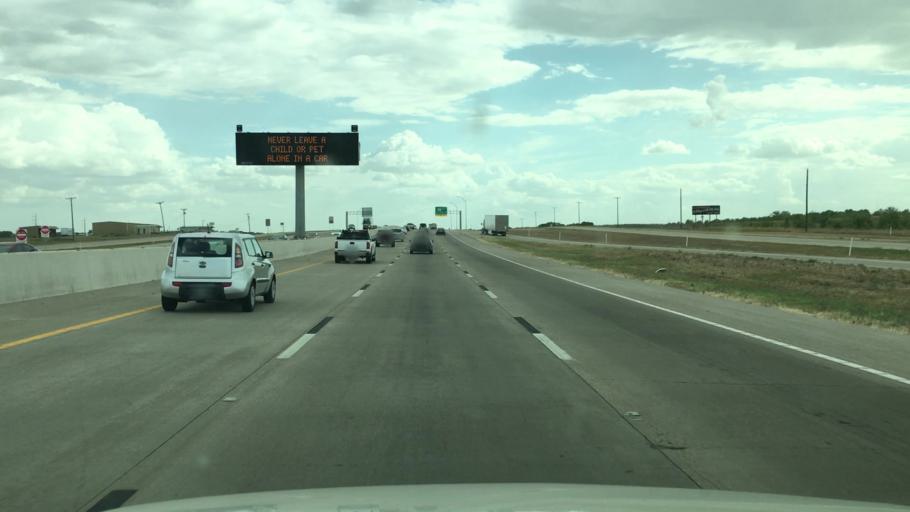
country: US
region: Texas
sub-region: McLennan County
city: Lorena
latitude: 31.4115
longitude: -97.2011
